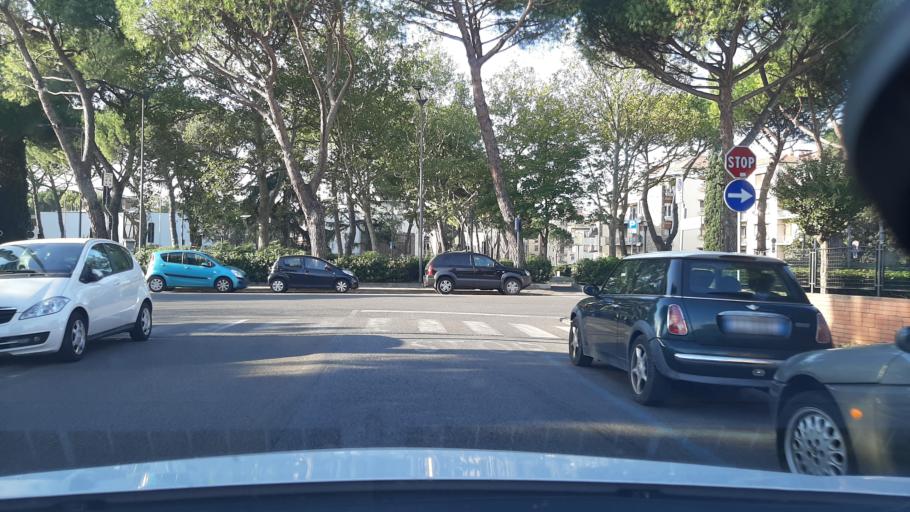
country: IT
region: Tuscany
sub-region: Province of Florence
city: Fiesole
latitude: 43.7834
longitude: 11.2922
